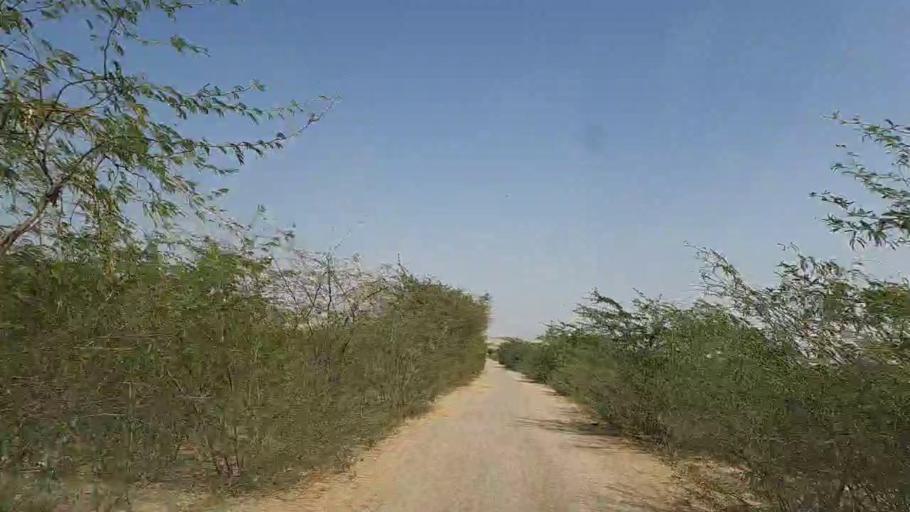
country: PK
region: Sindh
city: Naukot
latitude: 24.6291
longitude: 69.2889
